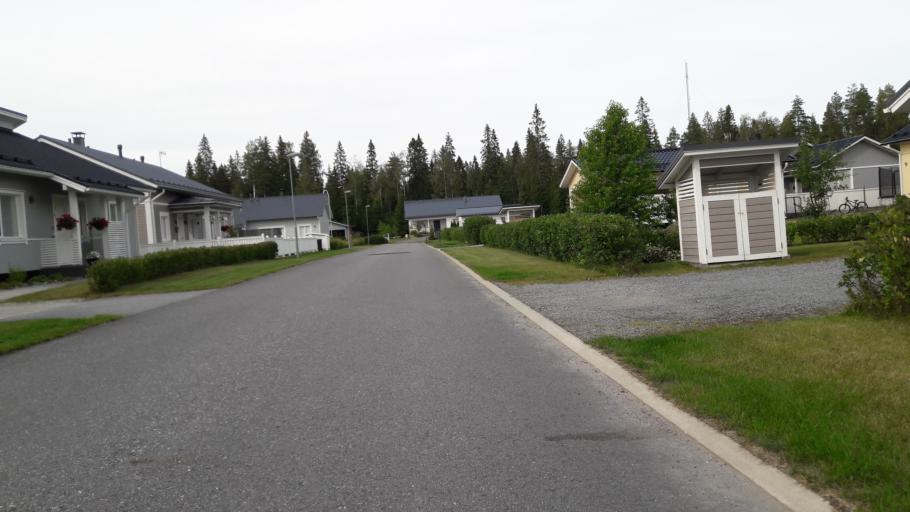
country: FI
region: North Karelia
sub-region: Joensuu
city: Joensuu
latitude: 62.5727
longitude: 29.8252
